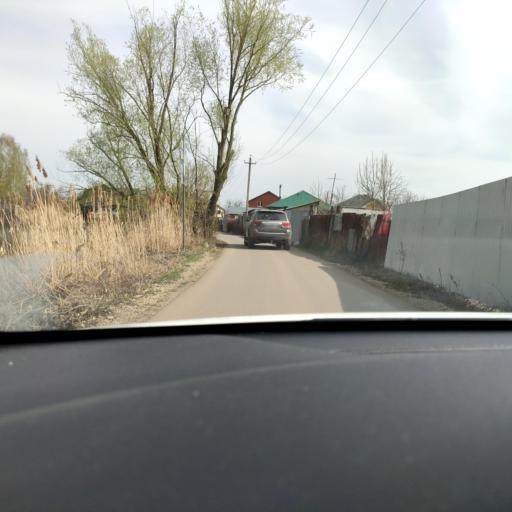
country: RU
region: Tatarstan
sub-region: Gorod Kazan'
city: Kazan
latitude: 55.8508
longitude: 49.1656
